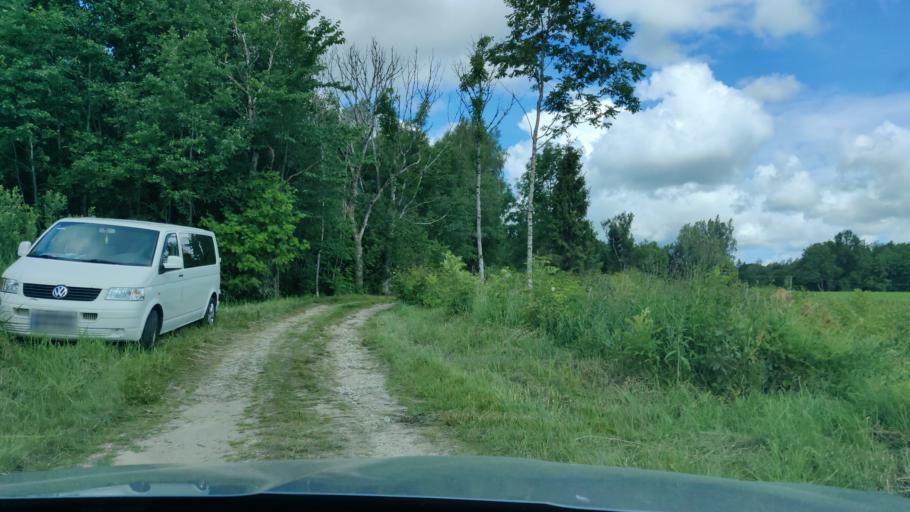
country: EE
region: Tartu
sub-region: Elva linn
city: Elva
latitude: 58.0267
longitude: 26.3440
